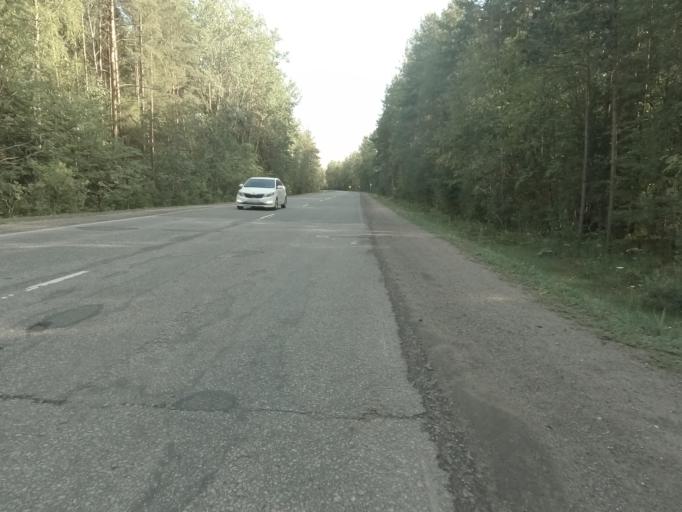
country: RU
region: Leningrad
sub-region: Volosovskiy Rayon
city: Shlissel'burg
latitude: 59.9419
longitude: 30.9833
